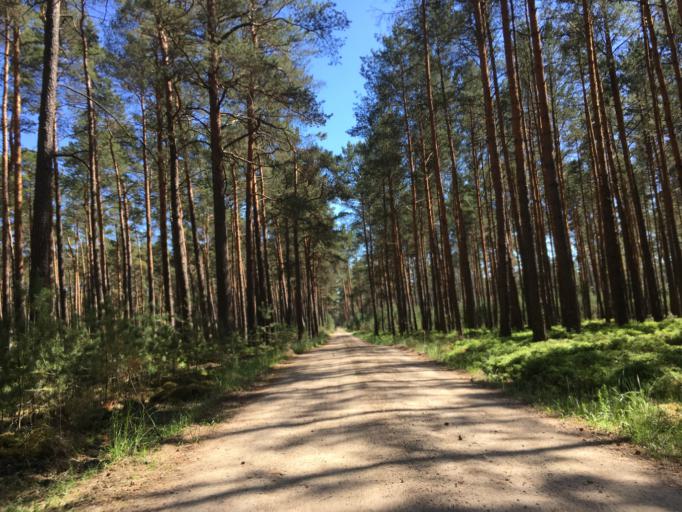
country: DE
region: Brandenburg
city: Friedrichswalde
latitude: 52.9704
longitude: 13.6348
